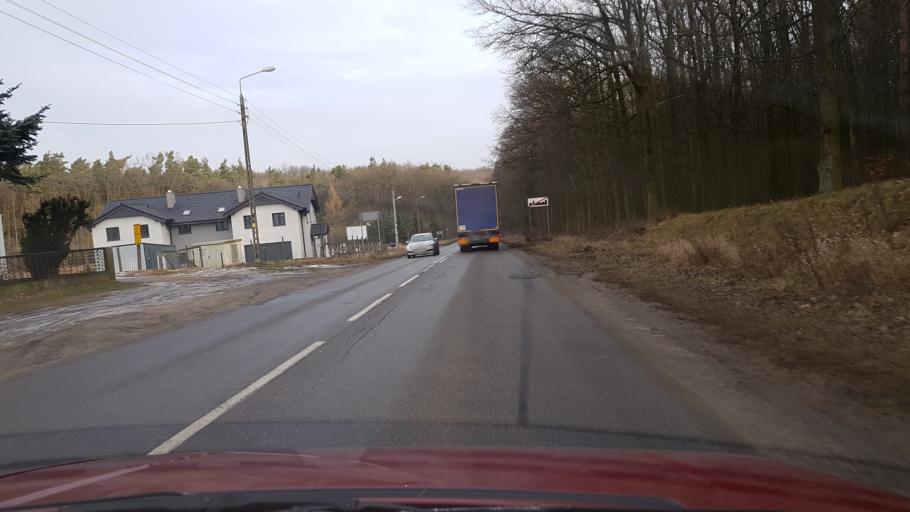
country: PL
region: West Pomeranian Voivodeship
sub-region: Powiat policki
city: Police
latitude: 53.5206
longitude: 14.5683
